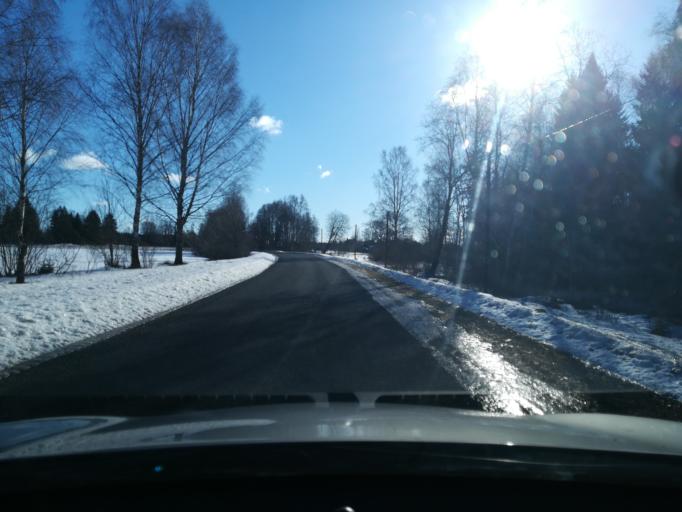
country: EE
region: Raplamaa
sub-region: Kohila vald
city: Kohila
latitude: 59.2400
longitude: 24.7522
